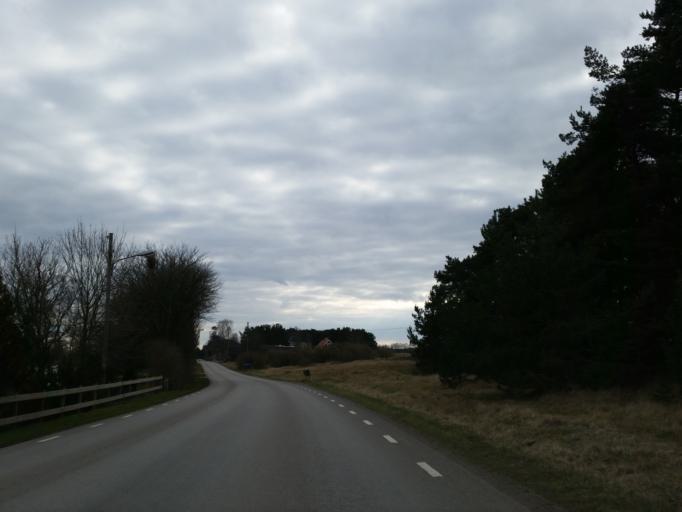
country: SE
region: Kalmar
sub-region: Morbylanga Kommun
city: Sodra Sandby
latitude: 56.5981
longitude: 16.6372
